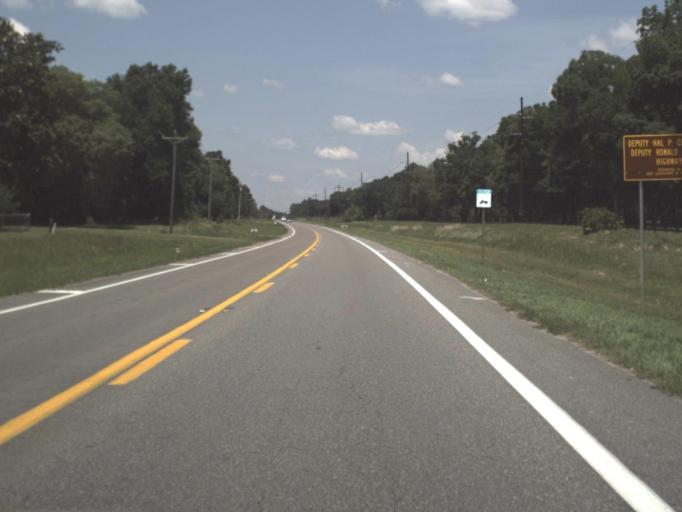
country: US
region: Florida
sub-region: Union County
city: Lake Butler
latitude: 30.0004
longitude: -82.2775
